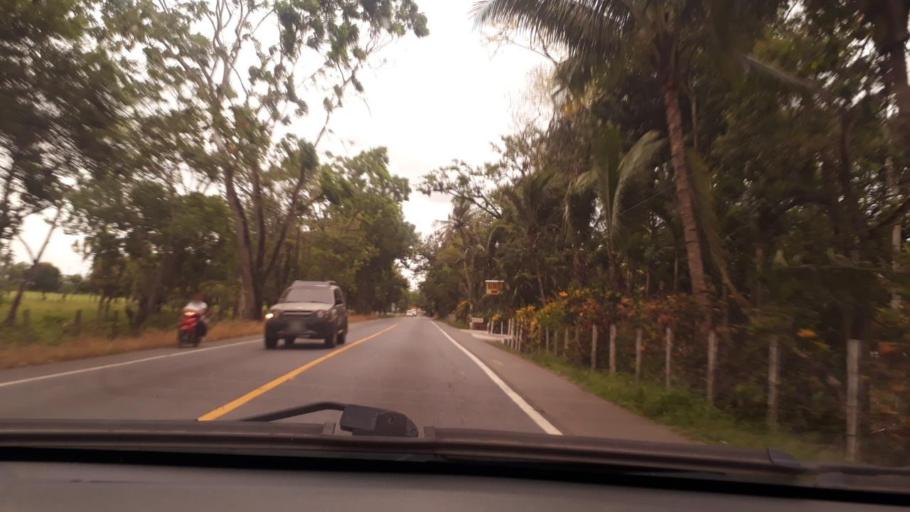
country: GT
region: Izabal
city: Morales
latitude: 15.4813
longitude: -88.8773
